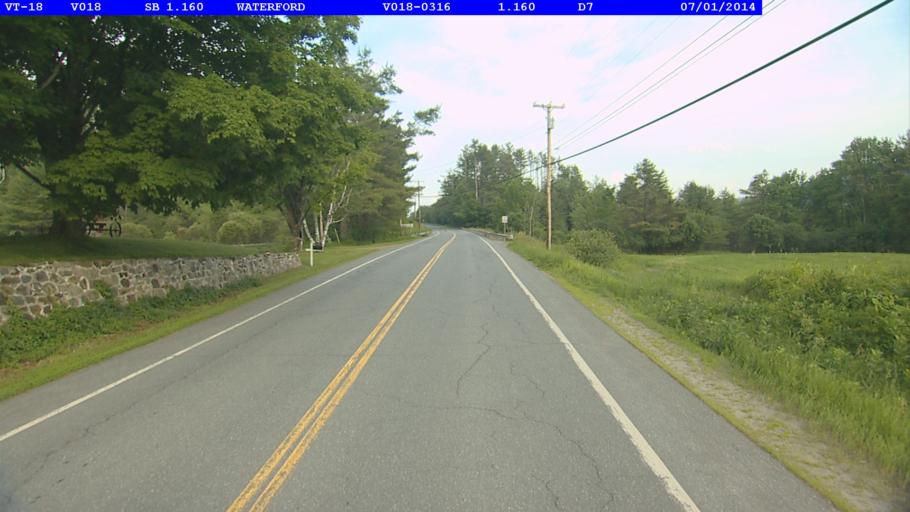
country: US
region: Vermont
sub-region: Caledonia County
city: Saint Johnsbury
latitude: 44.3541
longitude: -71.9051
